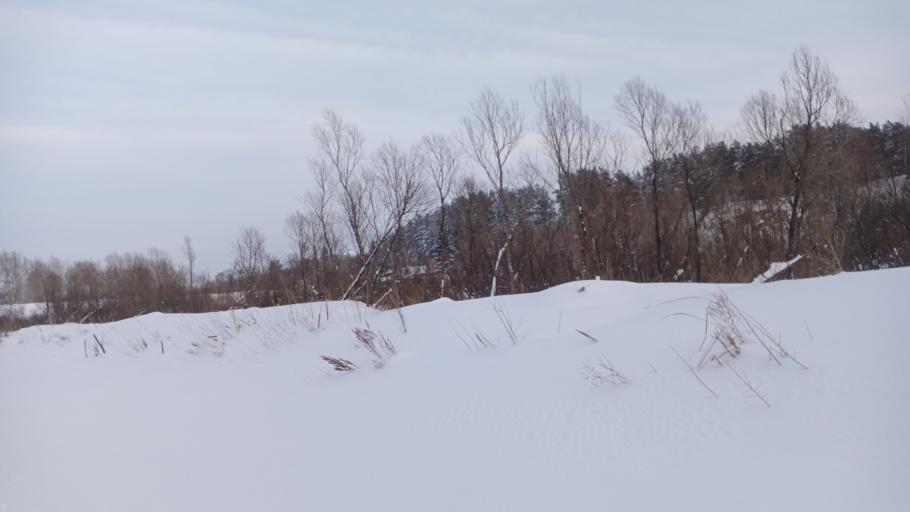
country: RU
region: Altai Krai
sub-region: Gorod Barnaulskiy
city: Barnaul
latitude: 53.3105
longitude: 83.7314
